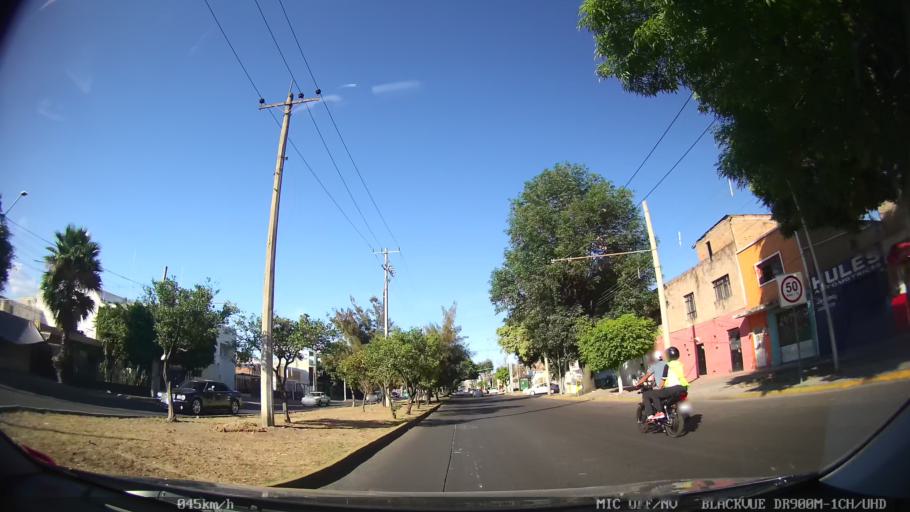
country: MX
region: Jalisco
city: Tlaquepaque
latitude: 20.6897
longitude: -103.3163
